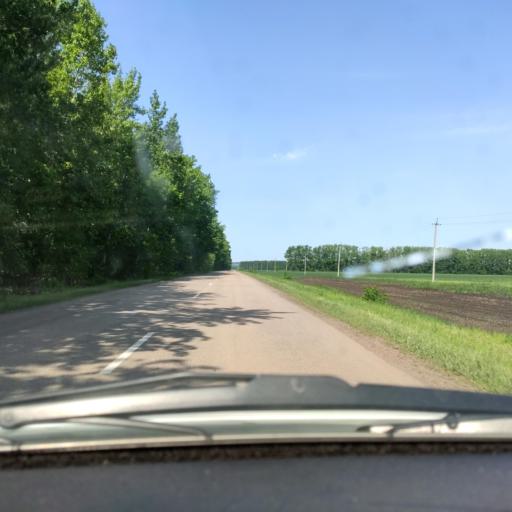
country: RU
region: Bashkortostan
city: Avdon
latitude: 54.5087
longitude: 55.6231
